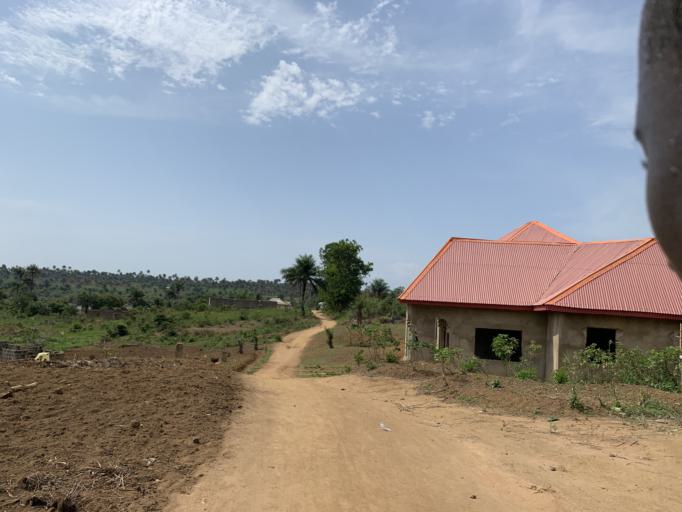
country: SL
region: Western Area
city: Waterloo
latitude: 8.3469
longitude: -13.0528
